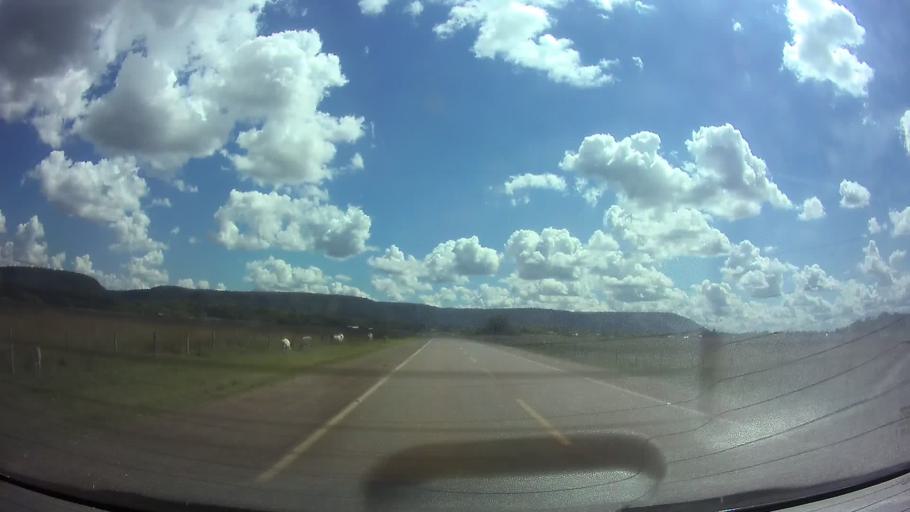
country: PY
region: Guaira
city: Itape
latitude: -25.9144
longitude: -56.6813
